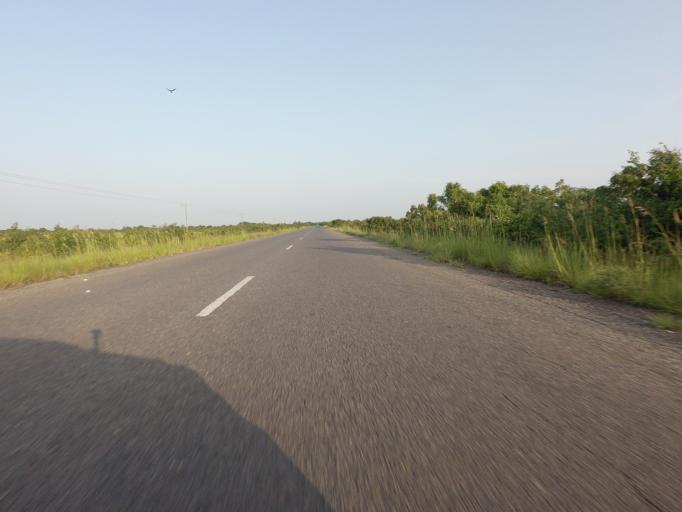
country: GH
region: Volta
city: Anloga
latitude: 5.9591
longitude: 0.6673
